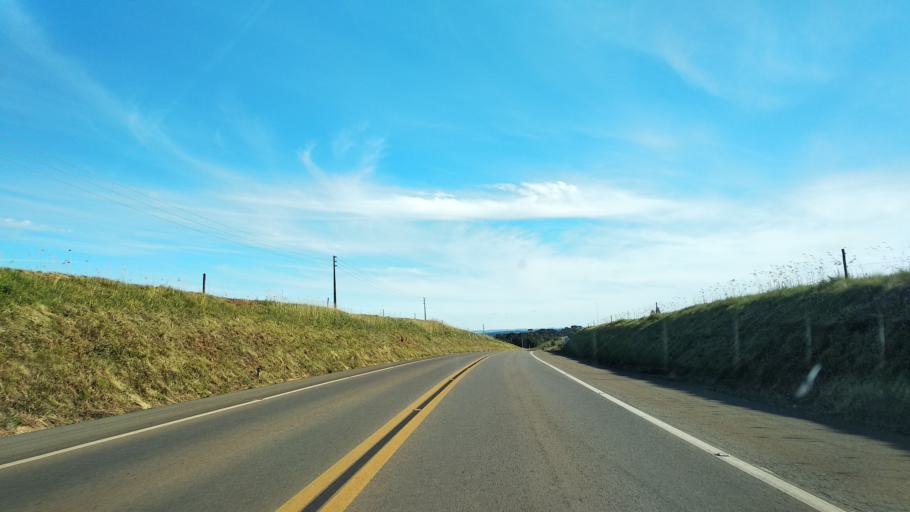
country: BR
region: Santa Catarina
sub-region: Celso Ramos
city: Celso Ramos
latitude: -27.5231
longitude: -51.3537
